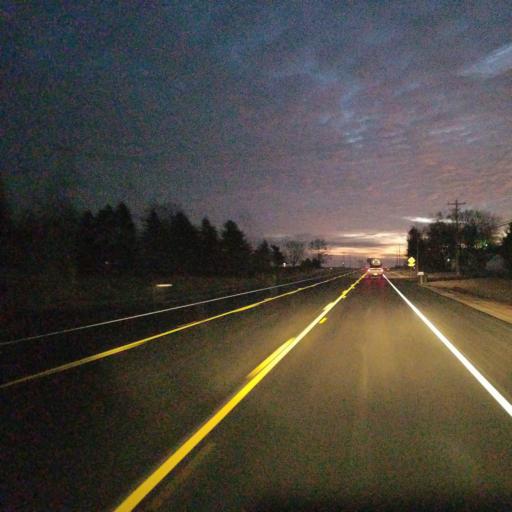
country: US
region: Illinois
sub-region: Peoria County
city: Hanna City
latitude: 40.6927
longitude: -89.7652
